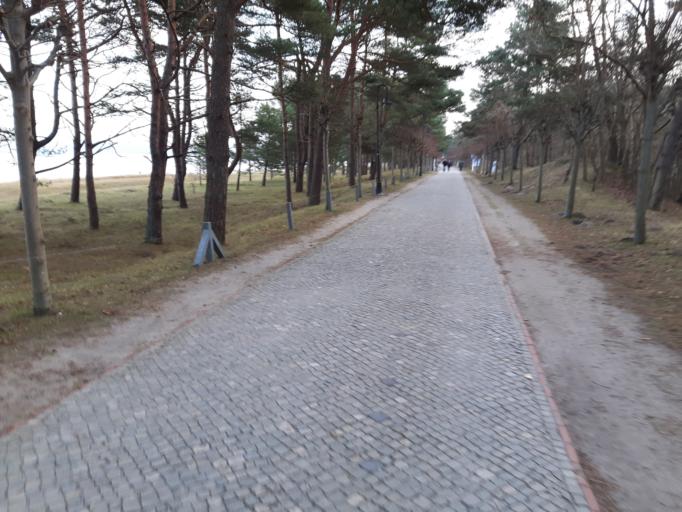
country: DE
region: Mecklenburg-Vorpommern
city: Ostseebad Binz
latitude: 54.4159
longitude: 13.5954
